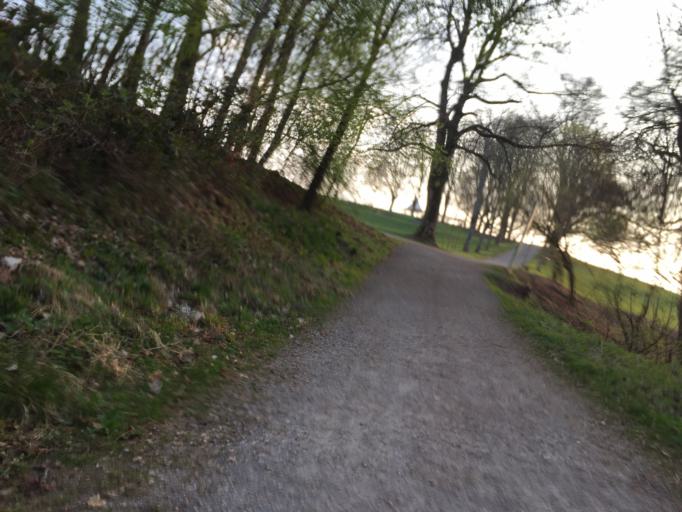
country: CH
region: Bern
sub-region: Bern-Mittelland District
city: Koniz
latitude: 46.9168
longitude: 7.4424
